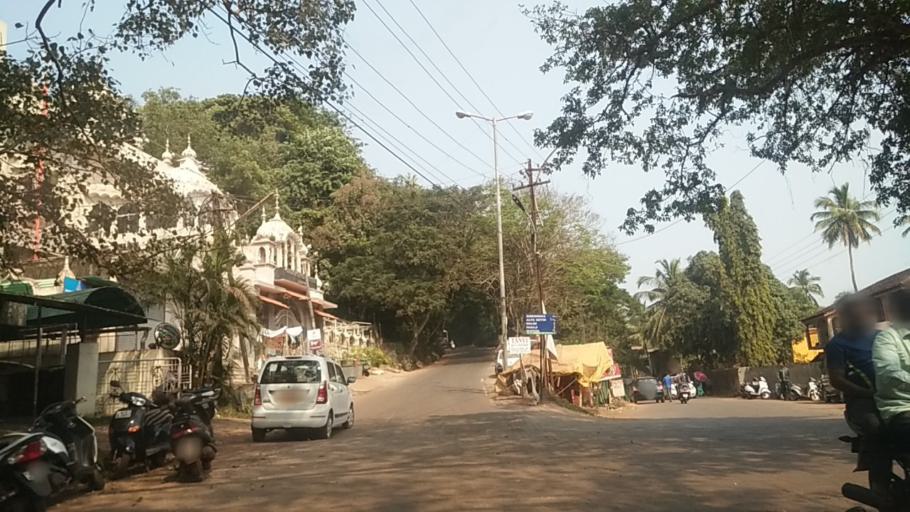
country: IN
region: Goa
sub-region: North Goa
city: Panaji
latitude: 15.5064
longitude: 73.8281
